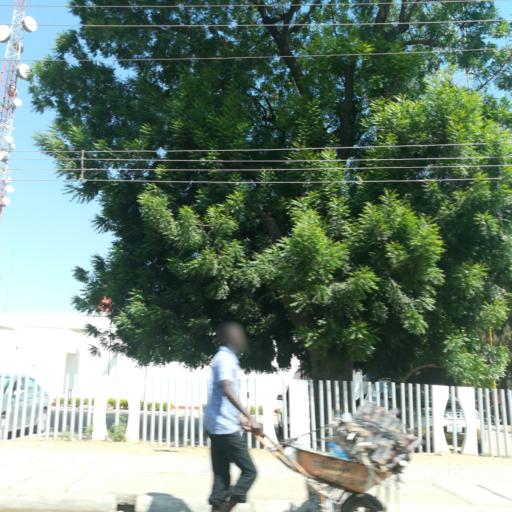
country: NG
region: Kano
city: Kano
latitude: 12.0051
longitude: 8.5399
